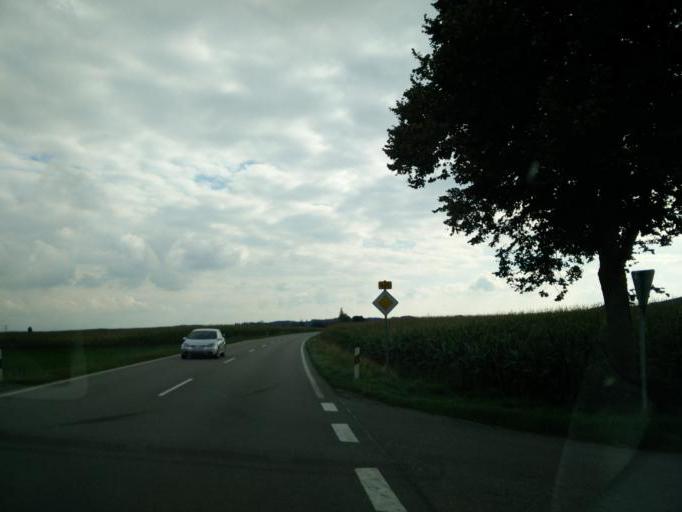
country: DE
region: Baden-Wuerttemberg
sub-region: Tuebingen Region
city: Bad Wurzach
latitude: 47.8814
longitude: 9.9101
